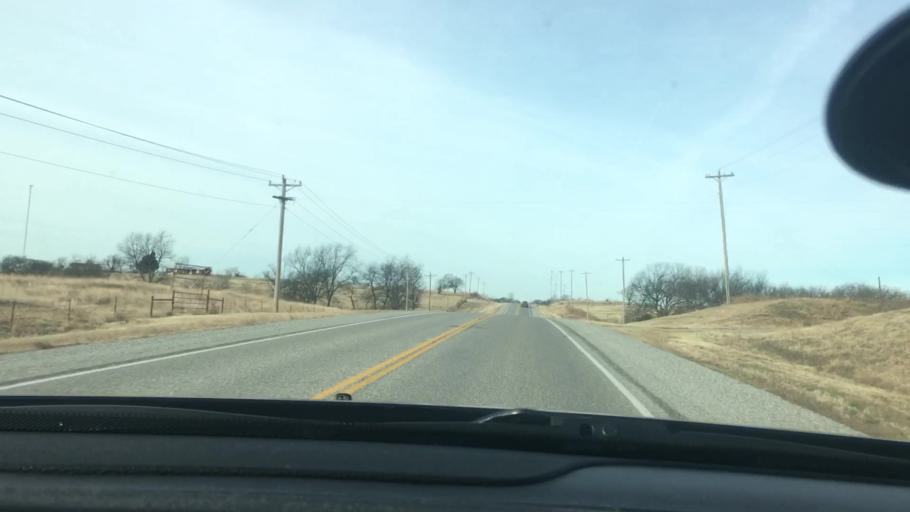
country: US
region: Oklahoma
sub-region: Garvin County
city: Stratford
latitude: 34.7967
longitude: -97.0273
